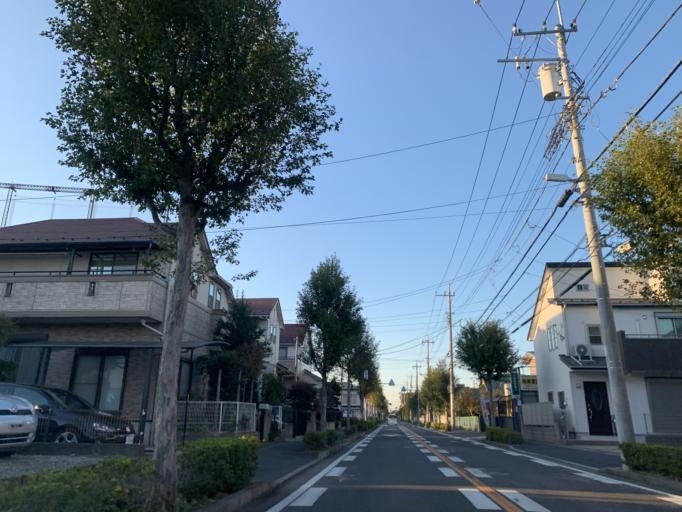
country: JP
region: Chiba
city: Nagareyama
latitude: 35.8892
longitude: 139.9178
